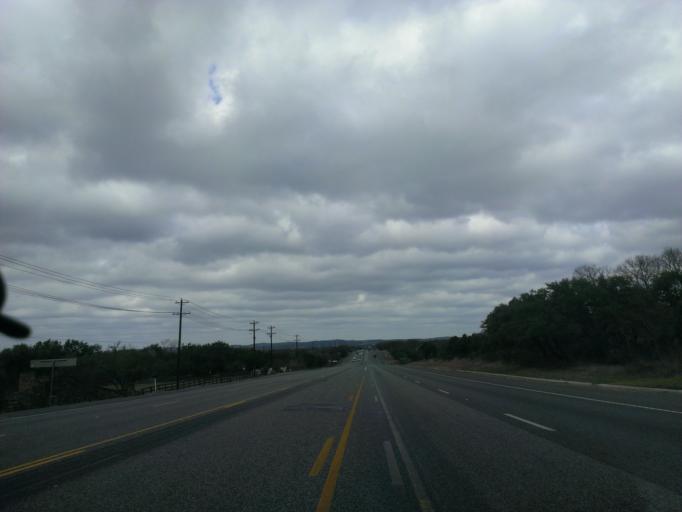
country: US
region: Texas
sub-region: Travis County
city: Briarcliff
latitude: 30.3754
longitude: -98.0796
